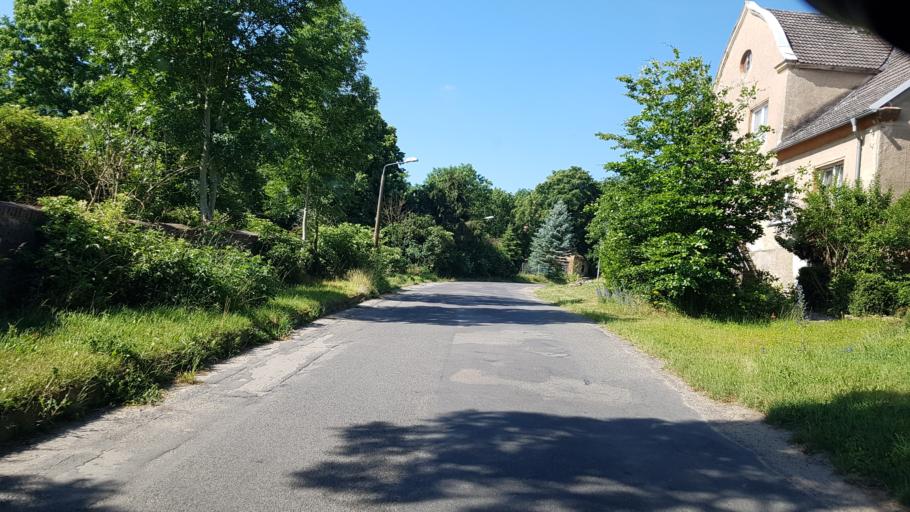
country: DE
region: Brandenburg
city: Gramzow
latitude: 53.2591
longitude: 13.9761
